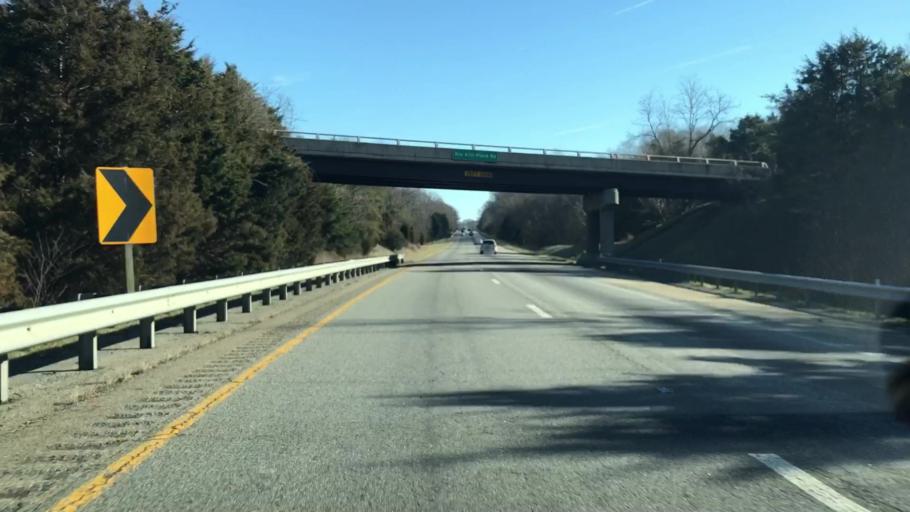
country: US
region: Virginia
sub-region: Botetourt County
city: Buchanan
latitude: 37.6107
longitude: -79.6096
